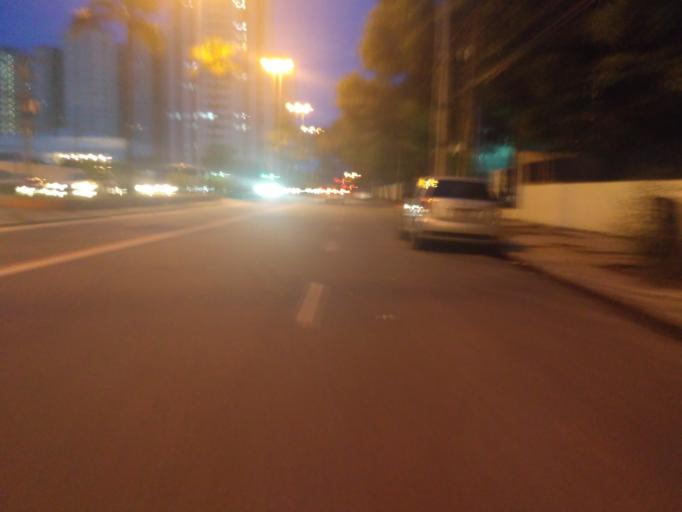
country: BR
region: Pernambuco
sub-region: Recife
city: Recife
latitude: -8.0548
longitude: -34.8804
